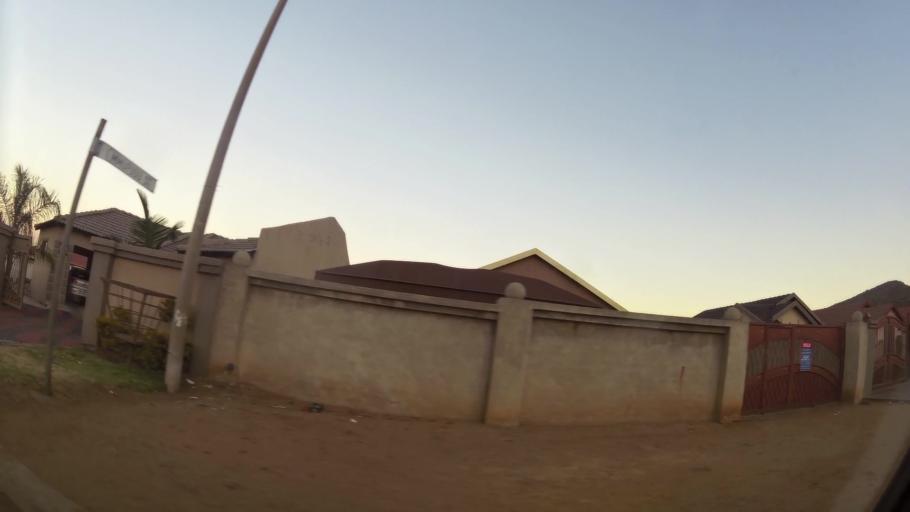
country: ZA
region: North-West
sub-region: Bojanala Platinum District Municipality
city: Rustenburg
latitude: -25.6421
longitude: 27.2006
